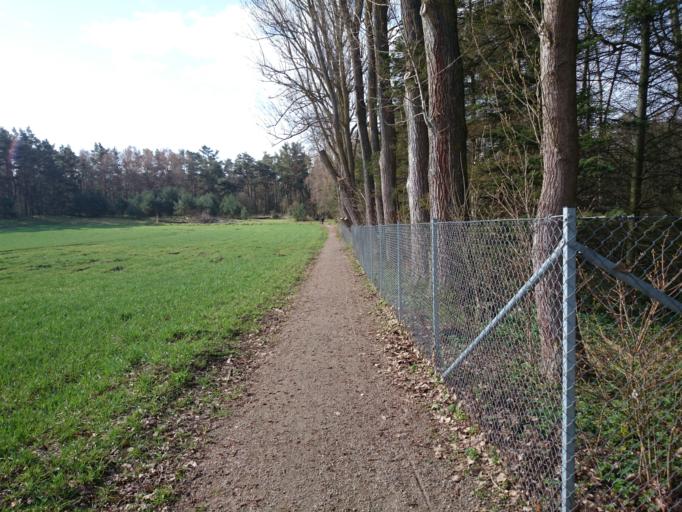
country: SE
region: Skane
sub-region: Landskrona
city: Asmundtorp
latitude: 55.8465
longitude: 12.9310
